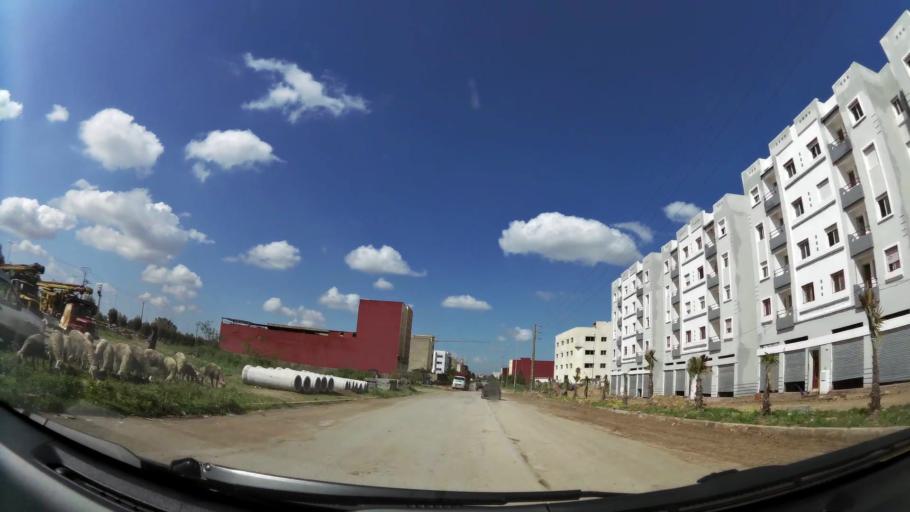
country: MA
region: Grand Casablanca
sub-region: Mediouna
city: Mediouna
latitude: 33.4441
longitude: -7.5199
